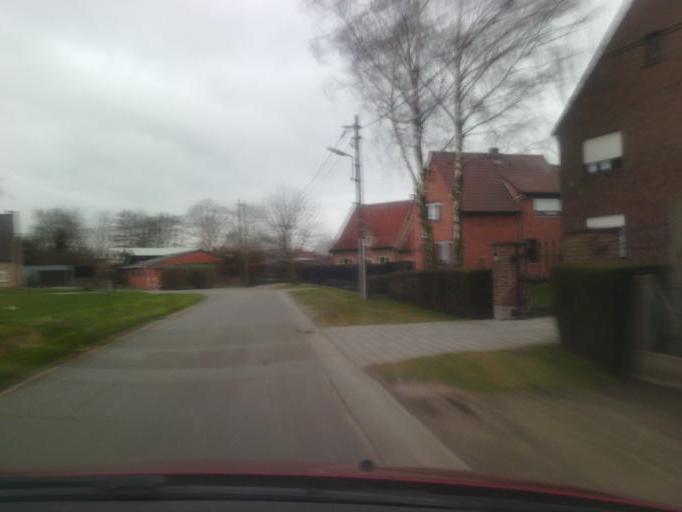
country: BE
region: Flanders
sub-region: Provincie Oost-Vlaanderen
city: Berlare
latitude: 51.0635
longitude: 4.0050
